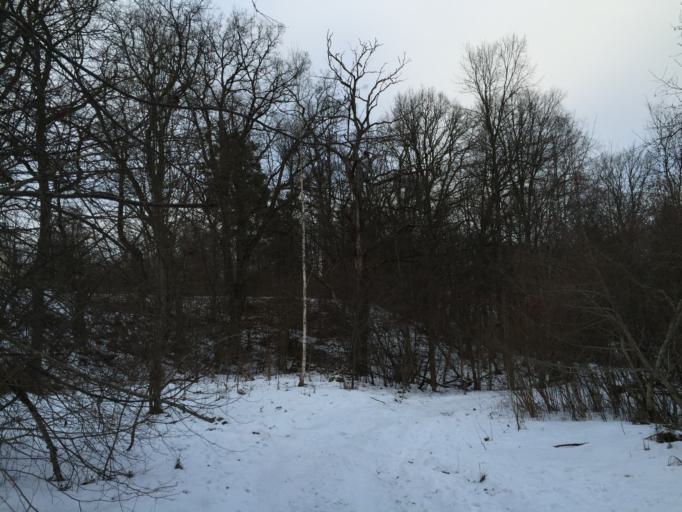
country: LV
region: Seja
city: Loja
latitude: 57.1314
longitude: 24.6659
